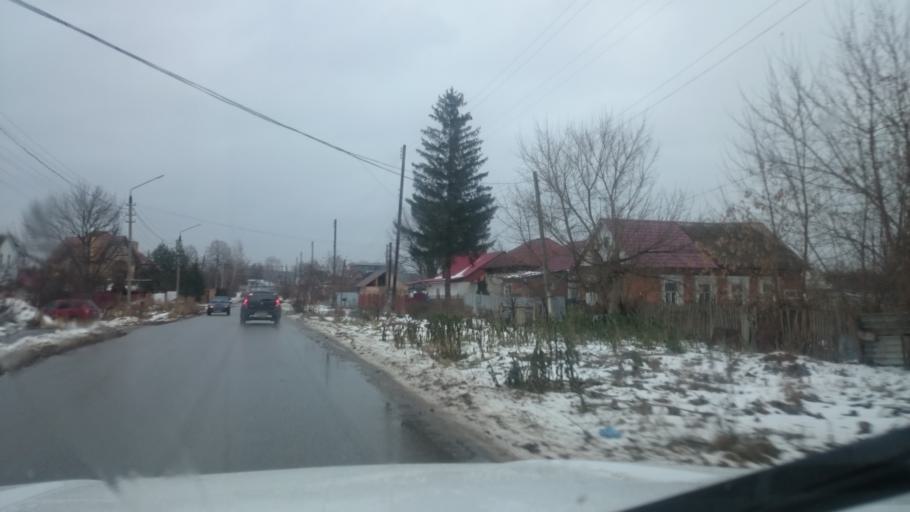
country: RU
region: Tula
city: Tula
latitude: 54.2047
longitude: 37.5609
